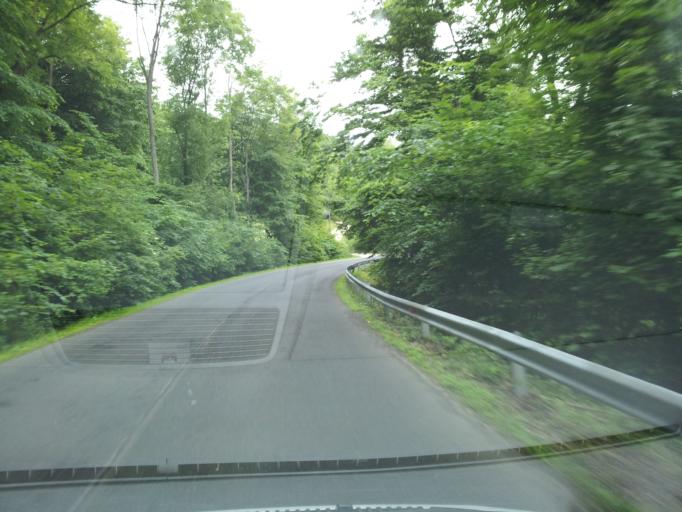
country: HU
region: Komarom-Esztergom
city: Kesztolc
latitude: 47.7266
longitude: 18.8363
